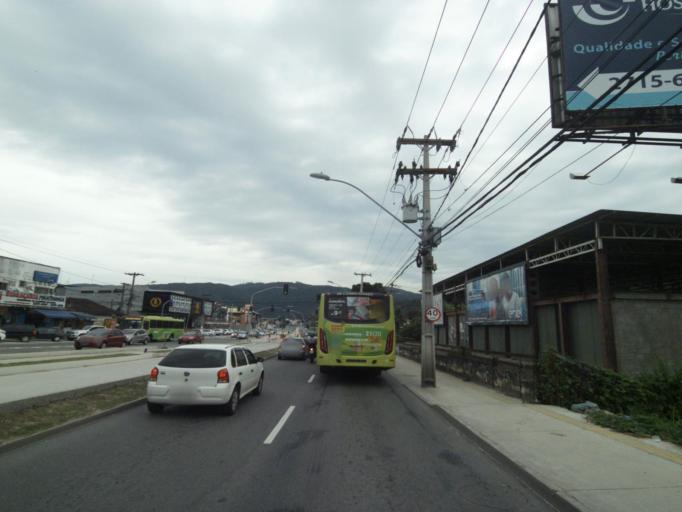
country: BR
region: Rio de Janeiro
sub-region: Niteroi
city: Niteroi
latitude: -22.9392
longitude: -43.0593
